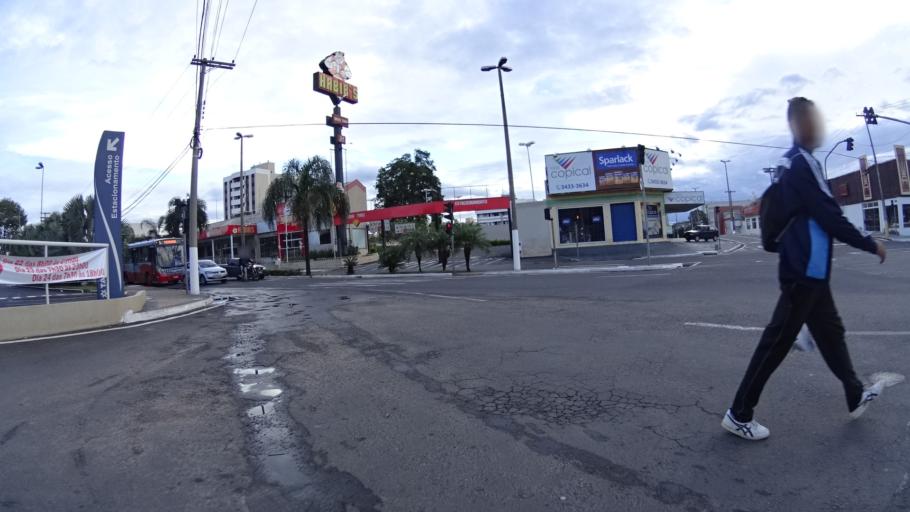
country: BR
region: Sao Paulo
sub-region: Marilia
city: Marilia
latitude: -22.2260
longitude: -49.9340
